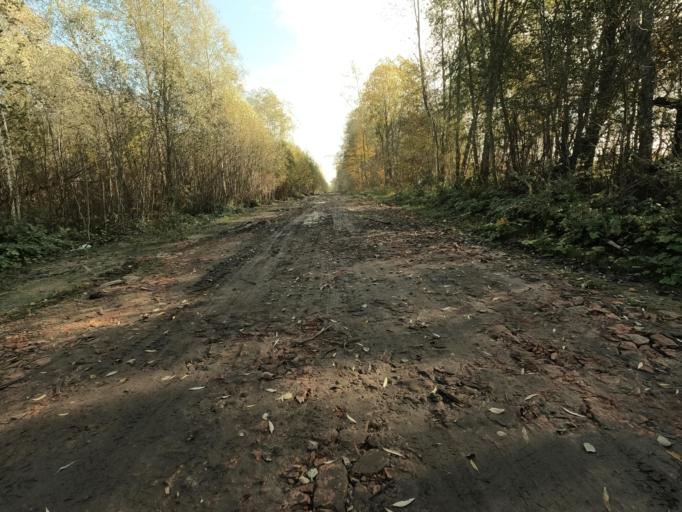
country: RU
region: Novgorod
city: Batetskiy
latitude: 58.8801
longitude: 30.7287
